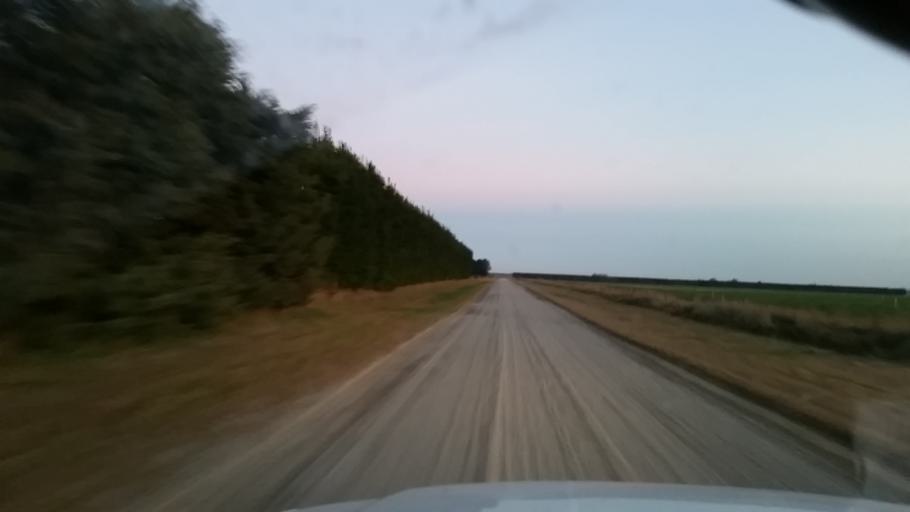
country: NZ
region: Canterbury
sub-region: Ashburton District
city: Tinwald
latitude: -43.9390
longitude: 171.6093
